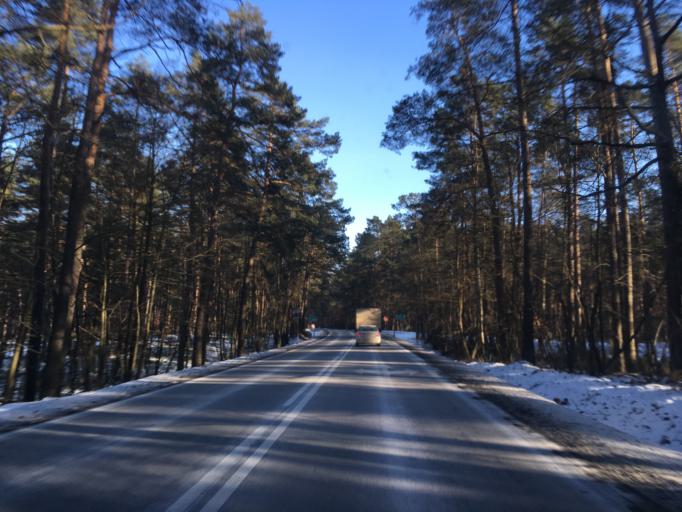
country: PL
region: Pomeranian Voivodeship
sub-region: Powiat koscierski
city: Koscierzyna
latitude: 54.1151
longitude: 17.8992
